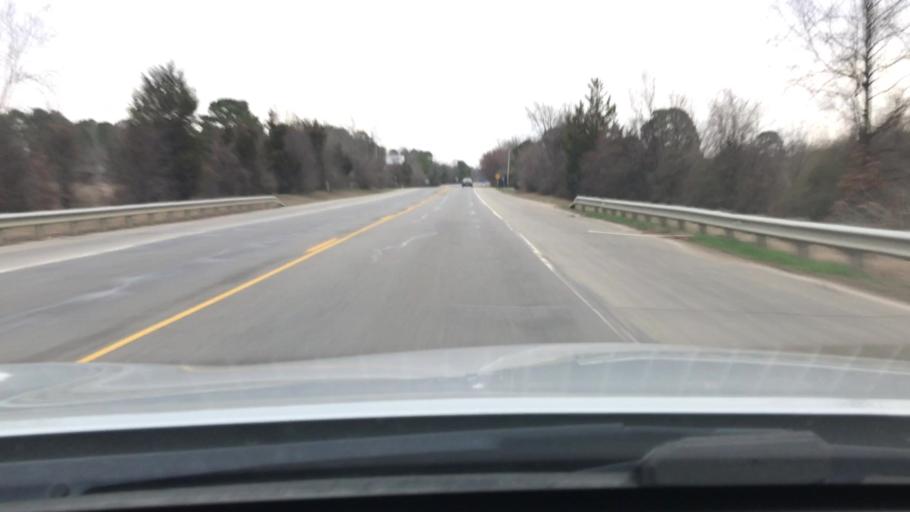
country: US
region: Arkansas
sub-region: Hempstead County
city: Hope
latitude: 33.6879
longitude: -93.5865
